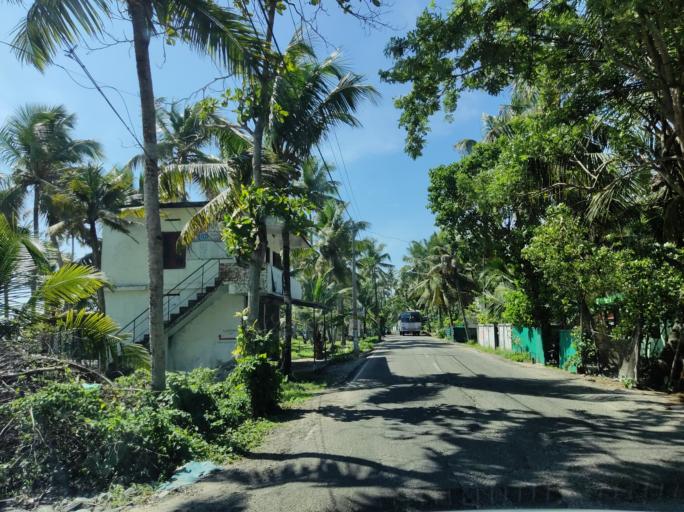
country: IN
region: Kerala
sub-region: Alappuzha
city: Kayankulam
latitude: 9.2386
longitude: 76.4166
